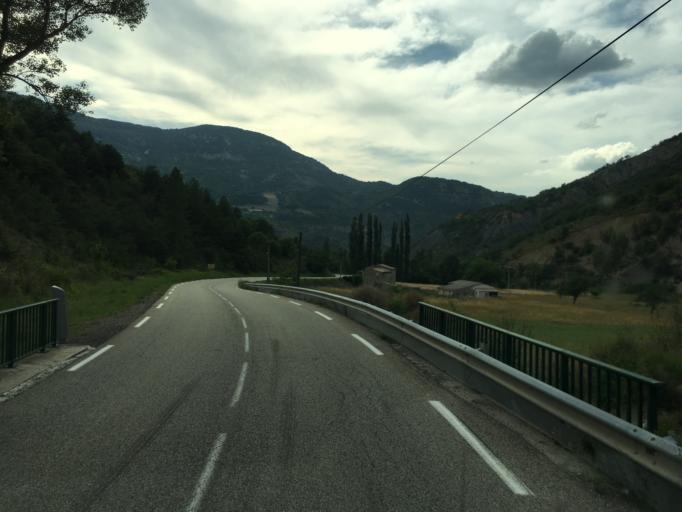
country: FR
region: Rhone-Alpes
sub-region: Departement de la Drome
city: Buis-les-Baronnies
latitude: 44.3923
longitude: 5.3676
